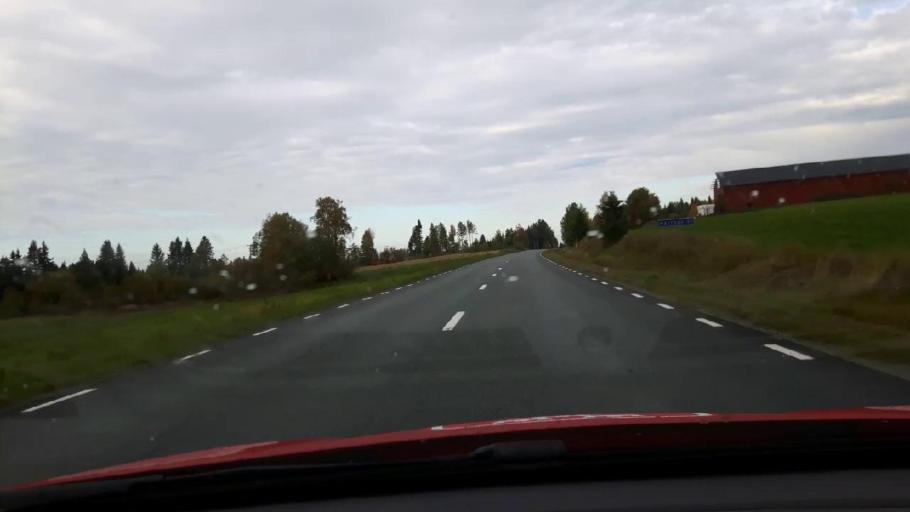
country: SE
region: Jaemtland
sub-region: Krokoms Kommun
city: Krokom
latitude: 63.1110
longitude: 14.2936
